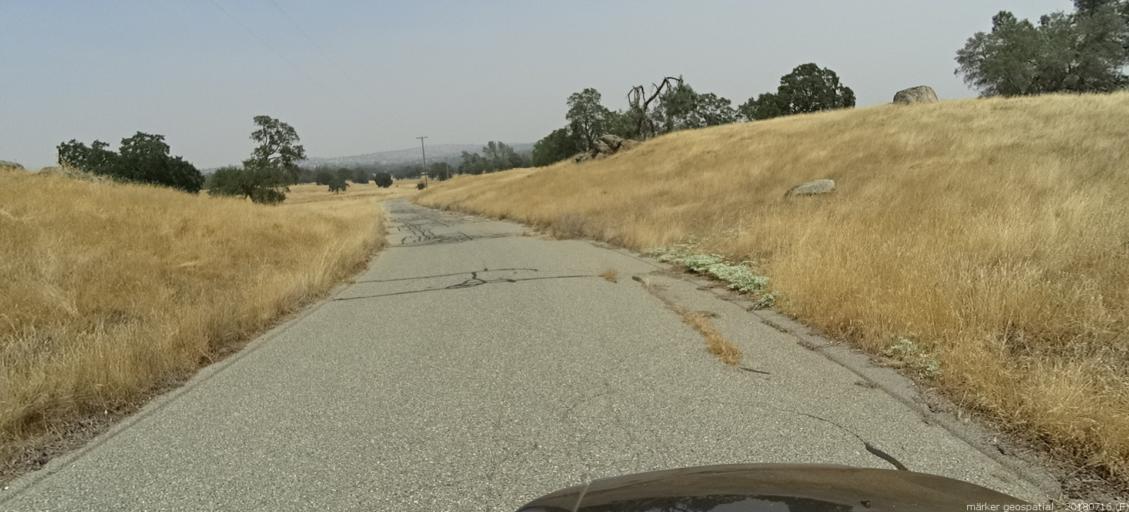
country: US
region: California
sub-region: Madera County
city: Yosemite Lakes
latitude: 37.1929
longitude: -119.9036
